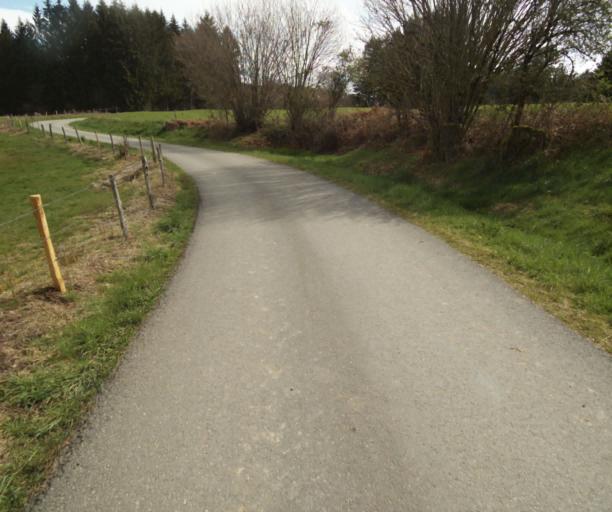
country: FR
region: Limousin
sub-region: Departement de la Correze
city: Egletons
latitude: 45.3623
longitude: 1.9730
